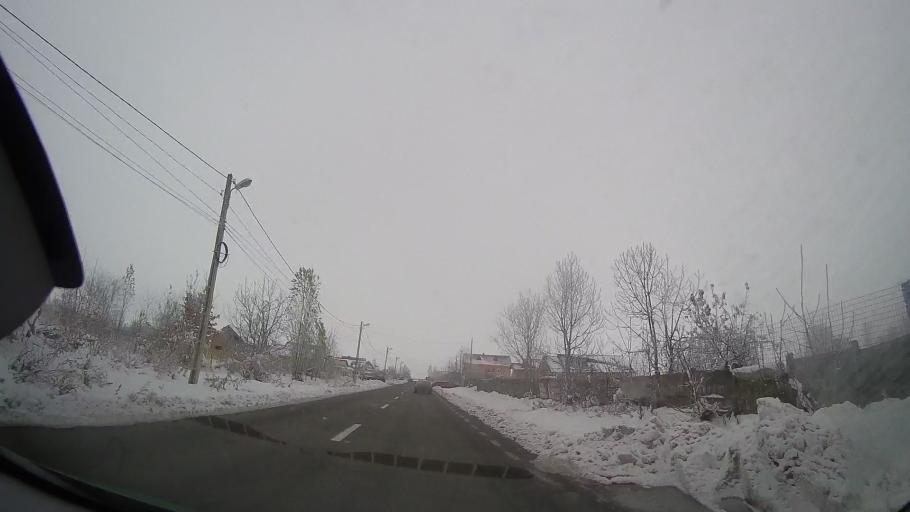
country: RO
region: Neamt
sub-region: Comuna Horia
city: Cotu Vames
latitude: 46.9356
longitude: 26.9450
